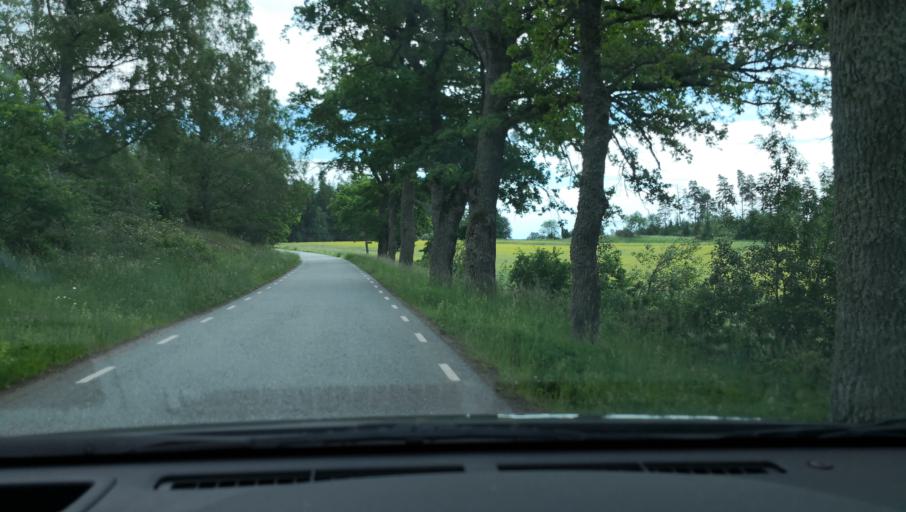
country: SE
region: Uppsala
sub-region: Enkopings Kommun
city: Orsundsbro
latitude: 59.7010
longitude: 17.4279
